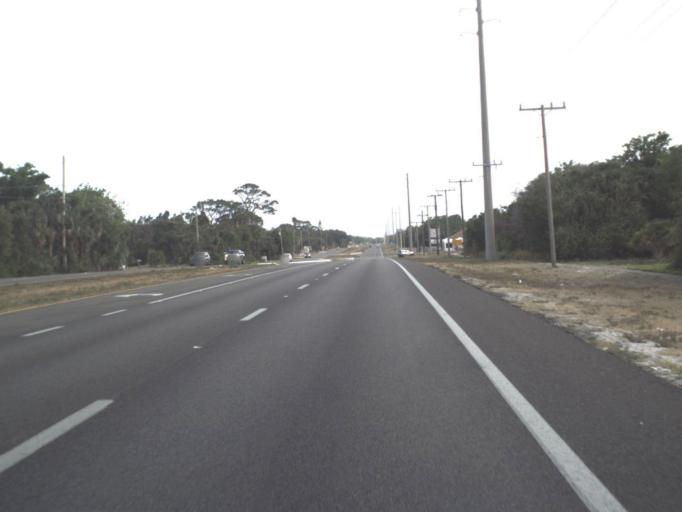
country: US
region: Florida
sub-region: Brevard County
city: Sharpes
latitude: 28.4581
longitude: -80.7631
